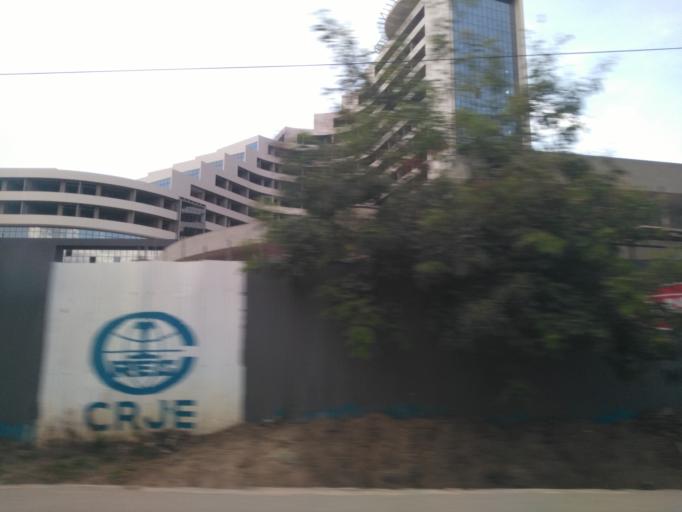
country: TZ
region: Mwanza
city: Mwanza
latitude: -2.5235
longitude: 32.8970
